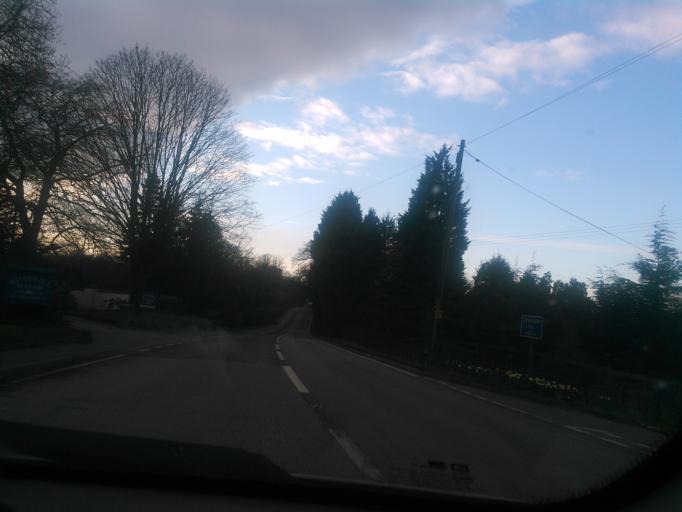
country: GB
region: England
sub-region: Shropshire
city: Stoke upon Tern
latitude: 52.8692
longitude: -2.5096
